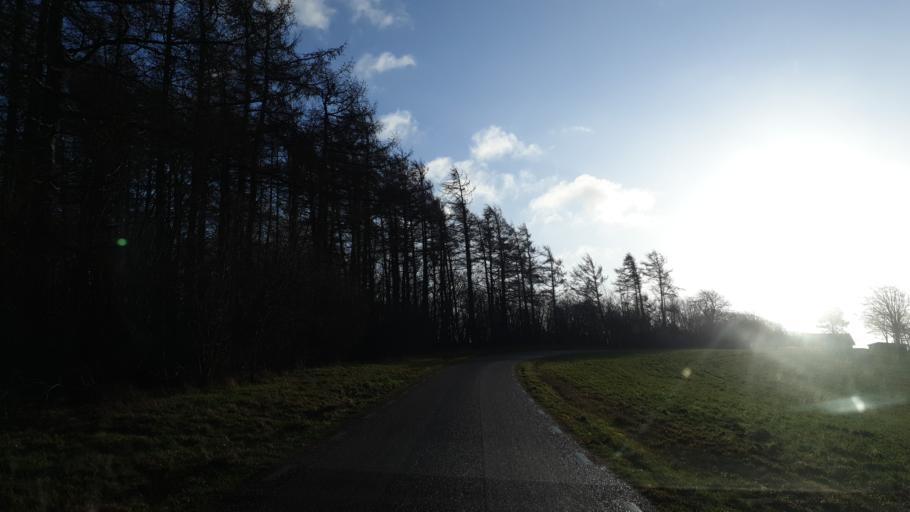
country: SE
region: Skane
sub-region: Svedala Kommun
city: Svedala
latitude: 55.4951
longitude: 13.2883
